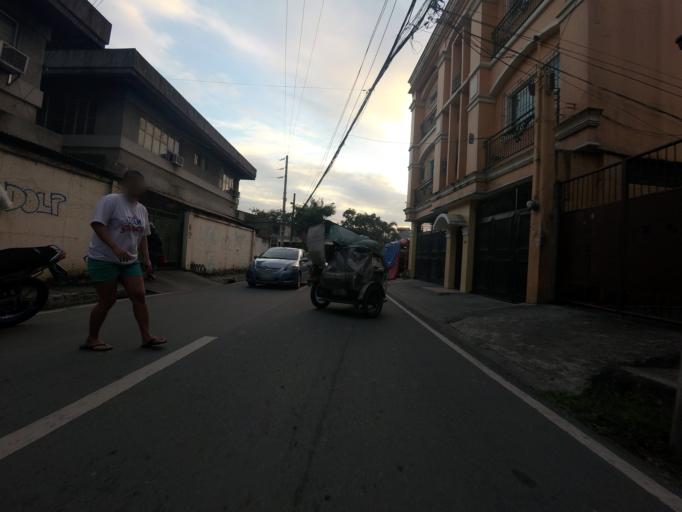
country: PH
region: Metro Manila
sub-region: San Juan
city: San Juan
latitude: 14.6007
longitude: 121.0335
